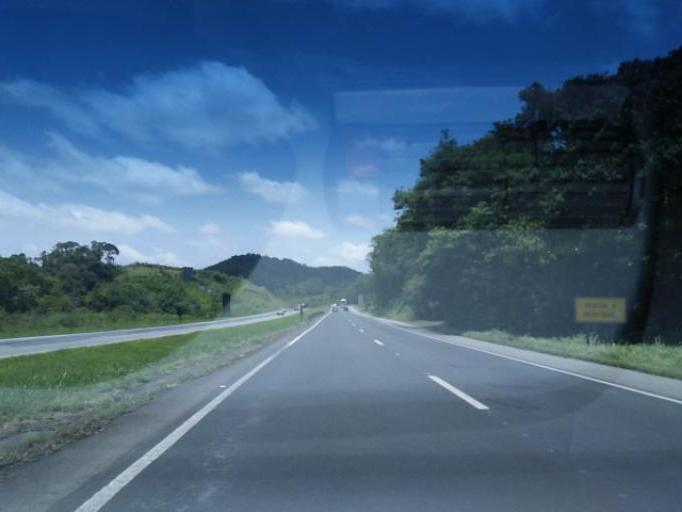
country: BR
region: Sao Paulo
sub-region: Juquia
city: Juquia
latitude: -24.3704
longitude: -47.7010
